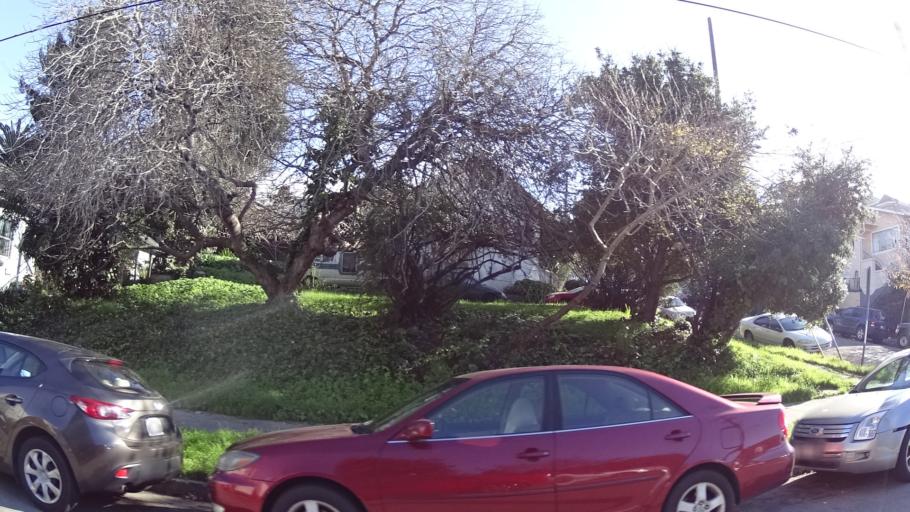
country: US
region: California
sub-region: Alameda County
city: Piedmont
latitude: 37.7968
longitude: -122.2311
